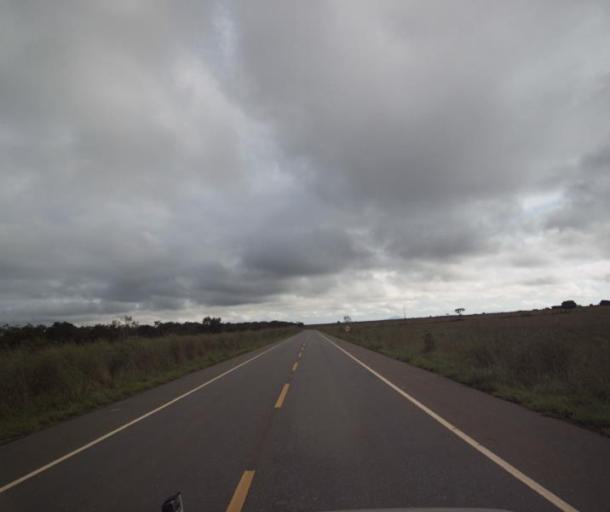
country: BR
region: Goias
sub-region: Padre Bernardo
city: Padre Bernardo
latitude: -15.3403
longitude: -48.6475
